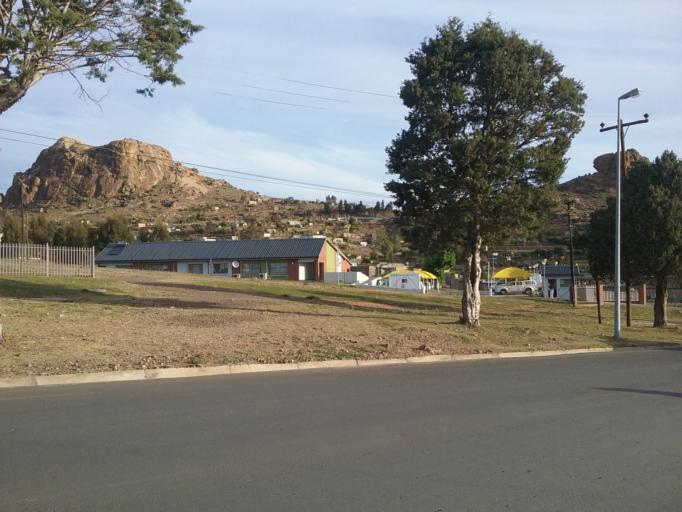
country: LS
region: Maseru
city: Maseru
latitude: -29.3463
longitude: 27.5256
